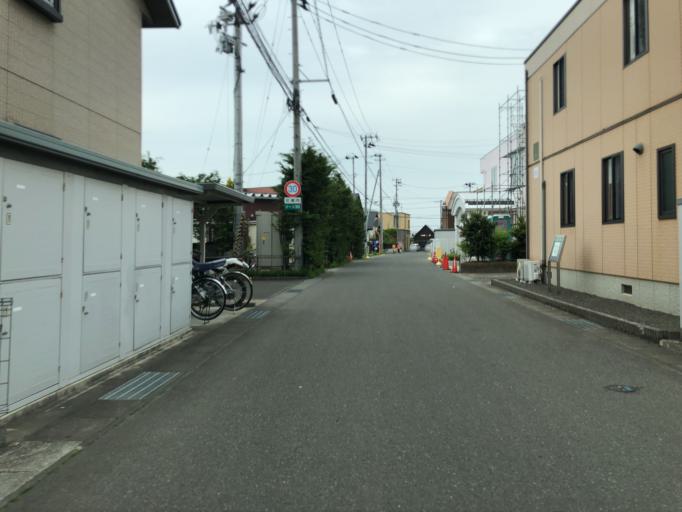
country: JP
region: Fukushima
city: Fukushima-shi
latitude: 37.7901
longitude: 140.4542
